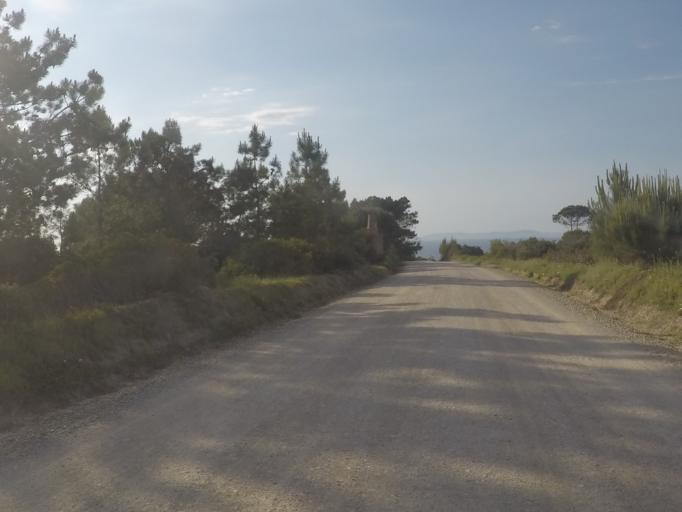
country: PT
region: Setubal
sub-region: Sesimbra
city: Sesimbra
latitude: 38.4473
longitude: -9.1990
